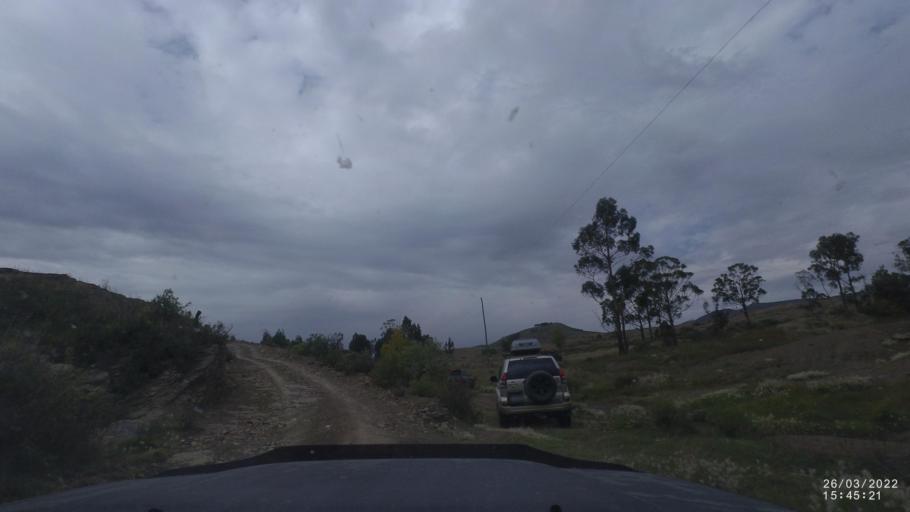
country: BO
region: Cochabamba
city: Cliza
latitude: -17.7478
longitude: -65.8581
